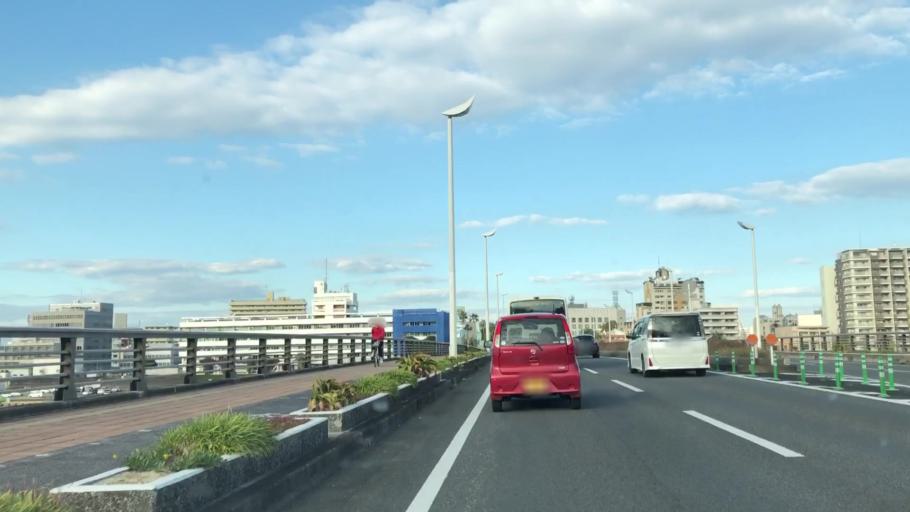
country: JP
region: Miyazaki
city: Miyazaki-shi
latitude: 31.9047
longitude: 131.4198
